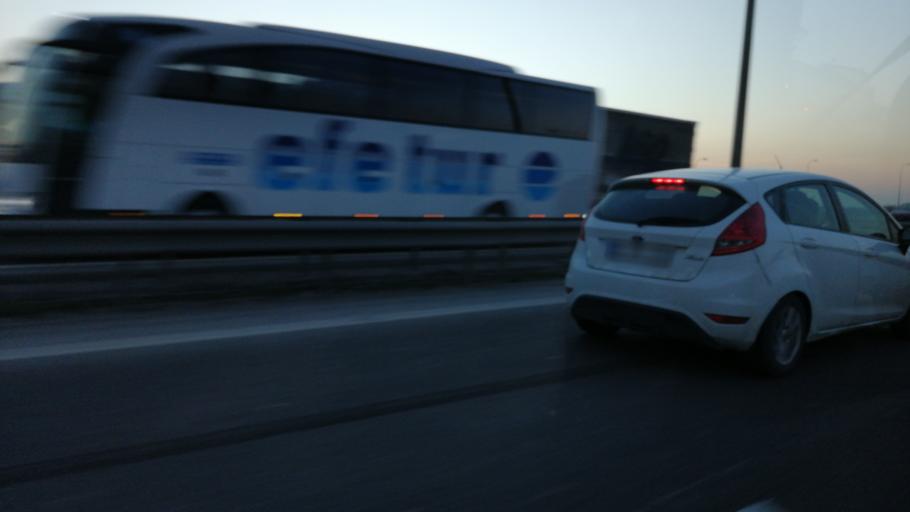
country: TR
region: Kocaeli
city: Balcik
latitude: 40.8798
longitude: 29.3826
